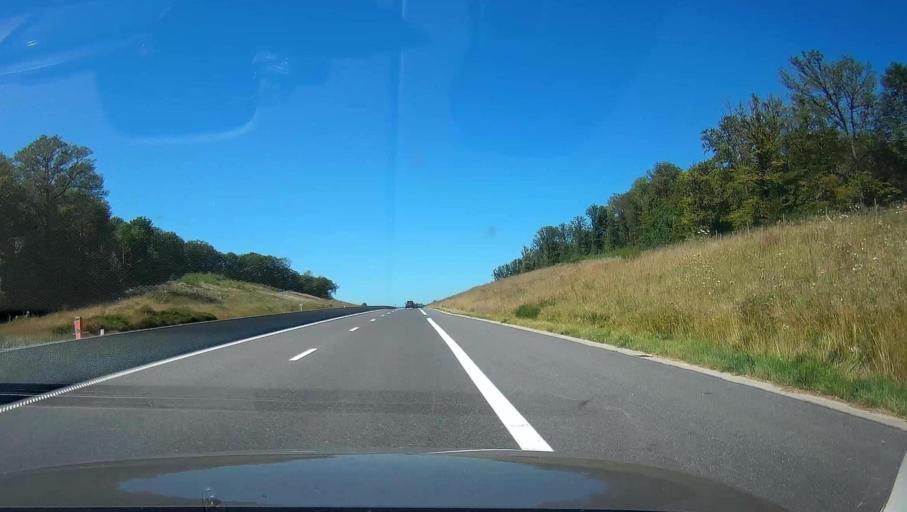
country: FR
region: Champagne-Ardenne
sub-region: Departement des Ardennes
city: Warcq
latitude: 49.7554
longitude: 4.6568
